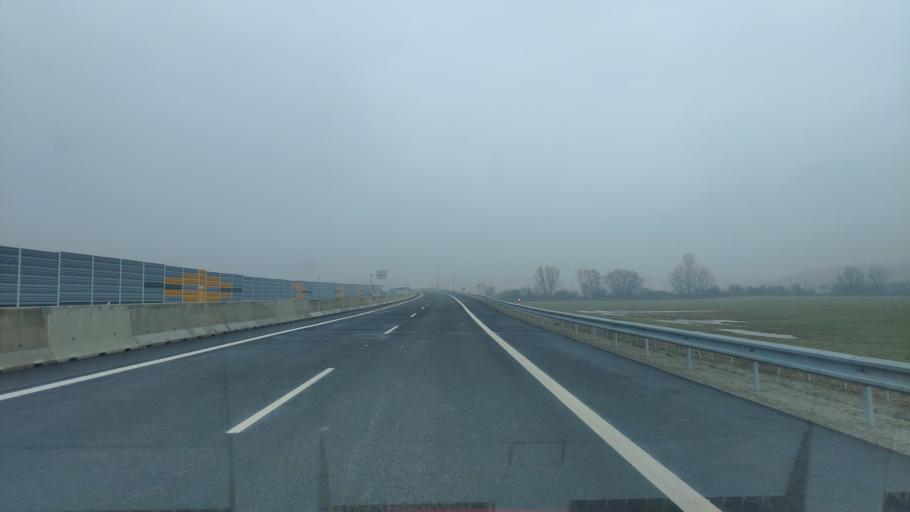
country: SK
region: Kosicky
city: Kosice
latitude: 48.7663
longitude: 21.3259
